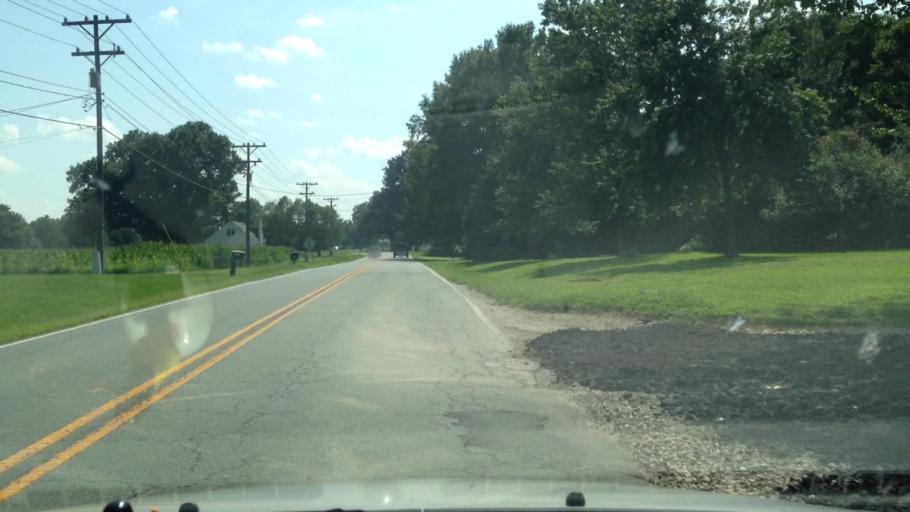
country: US
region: North Carolina
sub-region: Forsyth County
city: Kernersville
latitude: 36.1441
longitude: -80.0462
